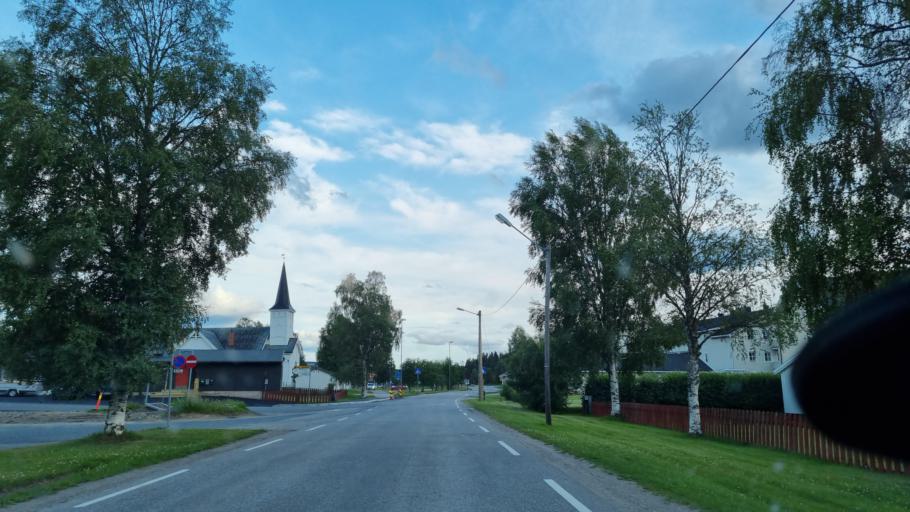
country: NO
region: Hedmark
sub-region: Trysil
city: Innbygda
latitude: 61.3184
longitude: 12.2600
